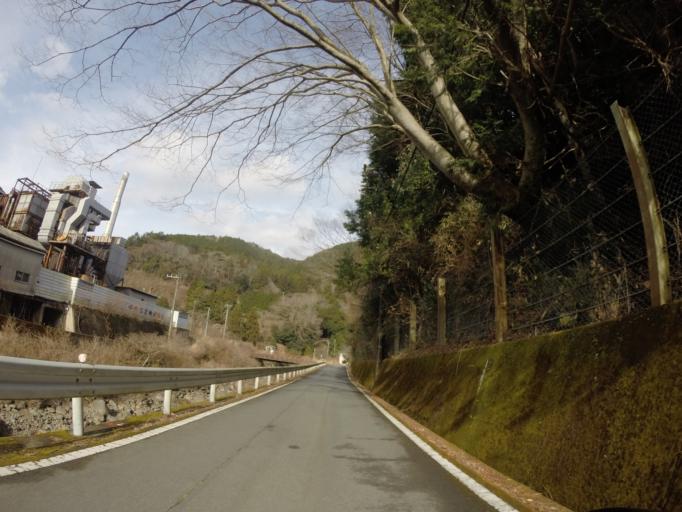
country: JP
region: Shizuoka
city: Heda
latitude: 34.8868
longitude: 138.8641
